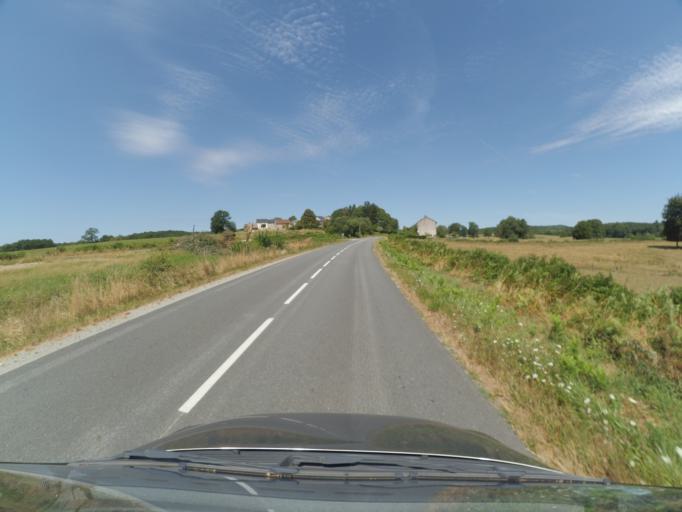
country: FR
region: Limousin
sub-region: Departement de la Creuse
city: Le Grand-Bourg
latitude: 46.0550
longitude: 1.6968
